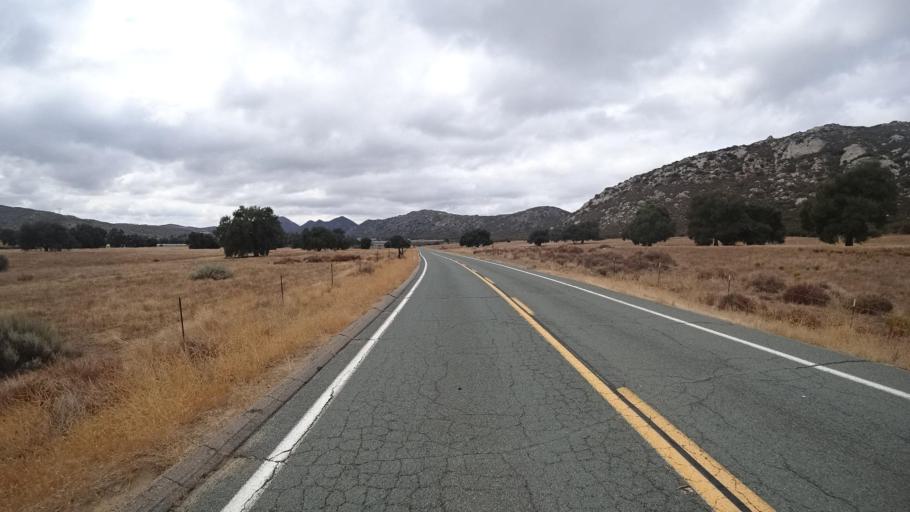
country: US
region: California
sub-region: San Diego County
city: Pine Valley
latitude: 32.7255
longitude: -116.4640
